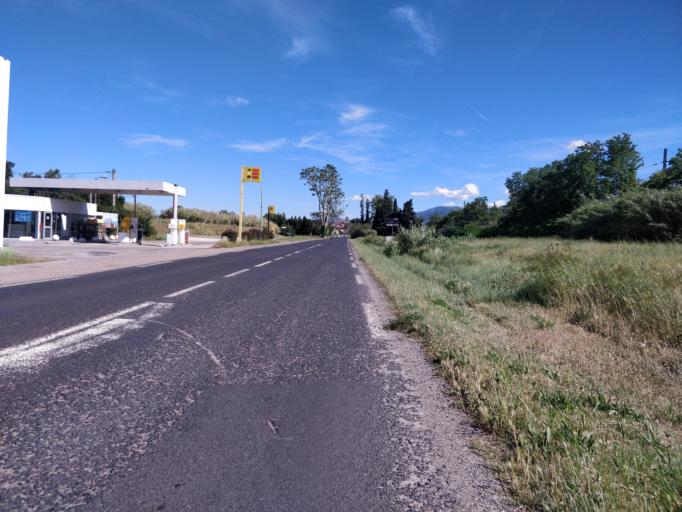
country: FR
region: Languedoc-Roussillon
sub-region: Departement des Pyrenees-Orientales
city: Elne
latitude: 42.6108
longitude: 2.9612
